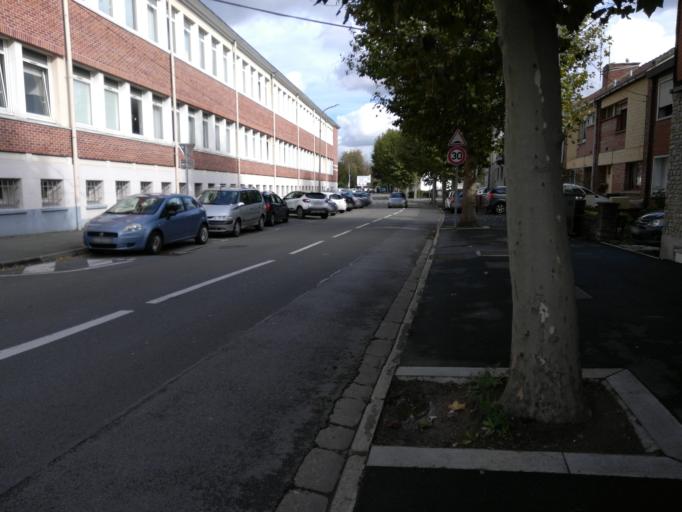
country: FR
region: Nord-Pas-de-Calais
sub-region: Departement du Pas-de-Calais
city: Montigny-en-Gohelle
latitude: 50.4301
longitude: 2.9464
